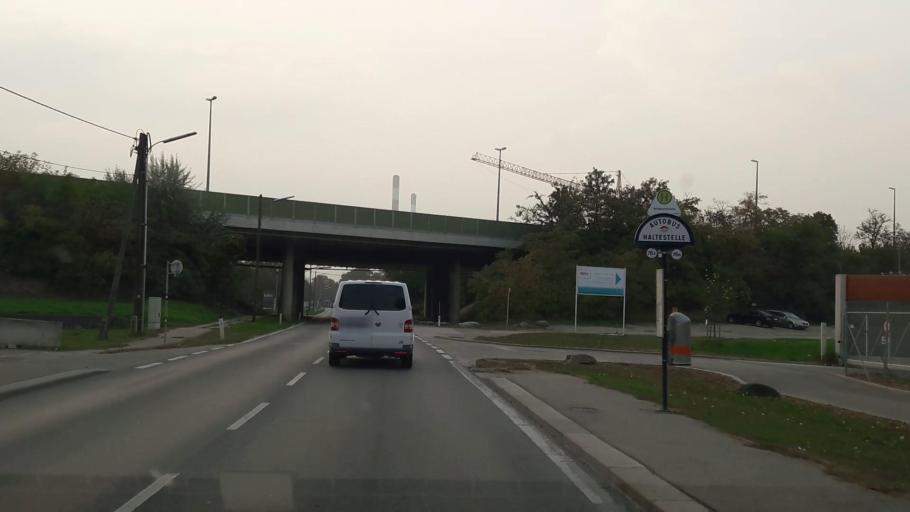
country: AT
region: Lower Austria
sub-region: Politischer Bezirk Wien-Umgebung
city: Schwechat
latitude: 48.1770
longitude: 16.4550
